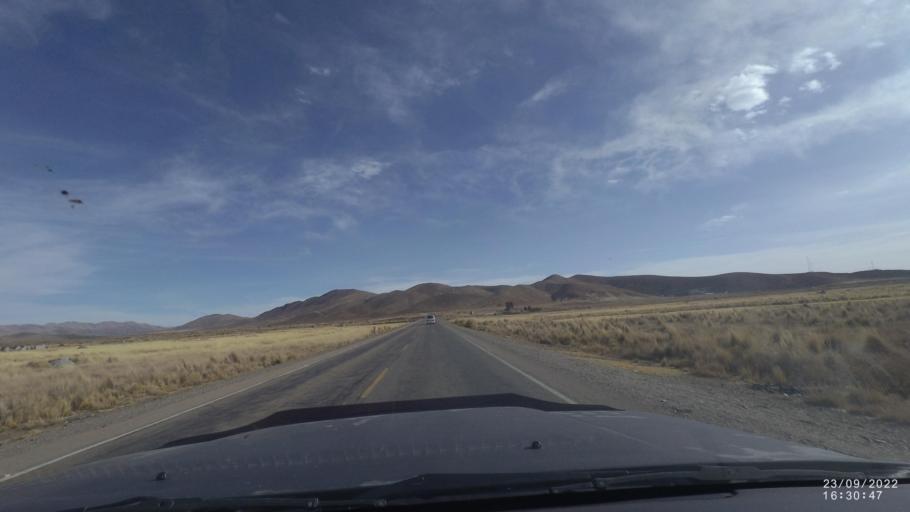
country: BO
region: Oruro
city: Machacamarca
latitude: -18.1588
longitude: -66.9866
